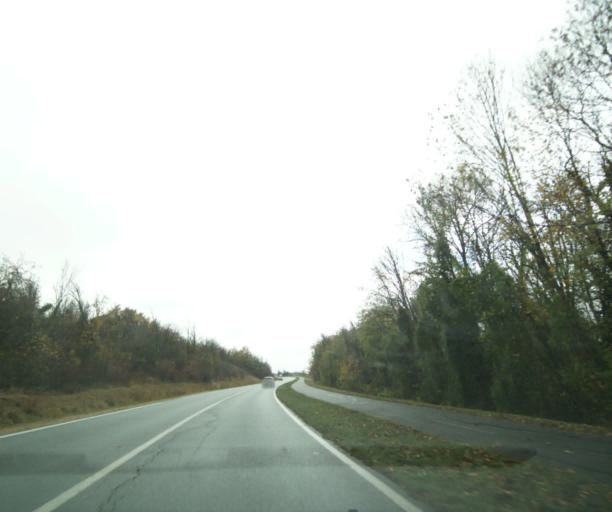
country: FR
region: Auvergne
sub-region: Departement du Puy-de-Dome
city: Cournon-d'Auvergne
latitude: 45.7489
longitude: 3.2110
